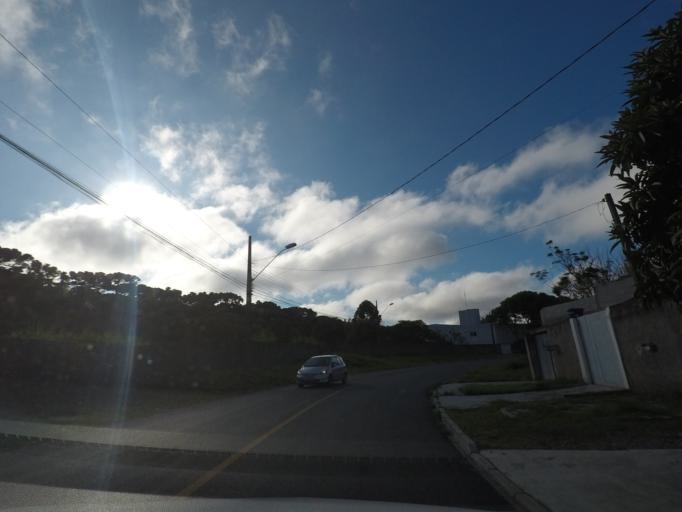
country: BR
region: Parana
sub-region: Curitiba
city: Curitiba
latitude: -25.4498
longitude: -49.2419
